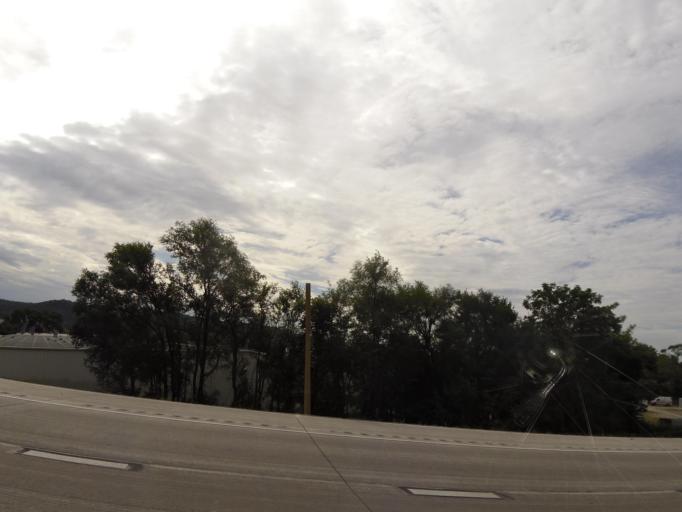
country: US
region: Wisconsin
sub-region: La Crosse County
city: Onalaska
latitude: 43.8681
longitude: -91.2249
